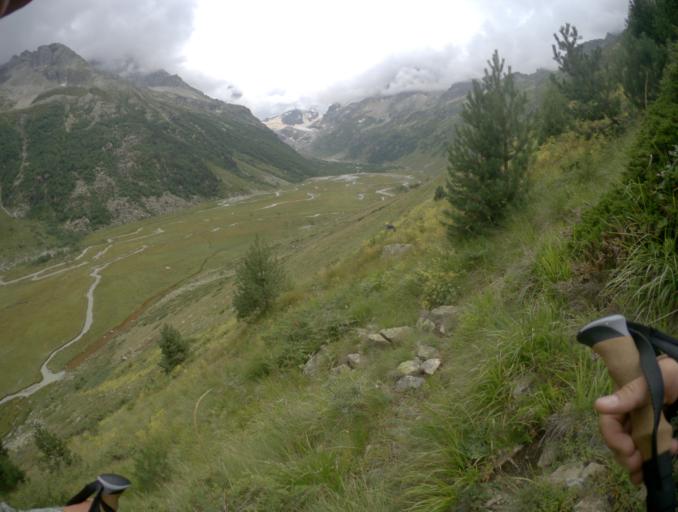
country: RU
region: Karachayevo-Cherkesiya
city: Uchkulan
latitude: 43.2675
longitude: 42.1393
